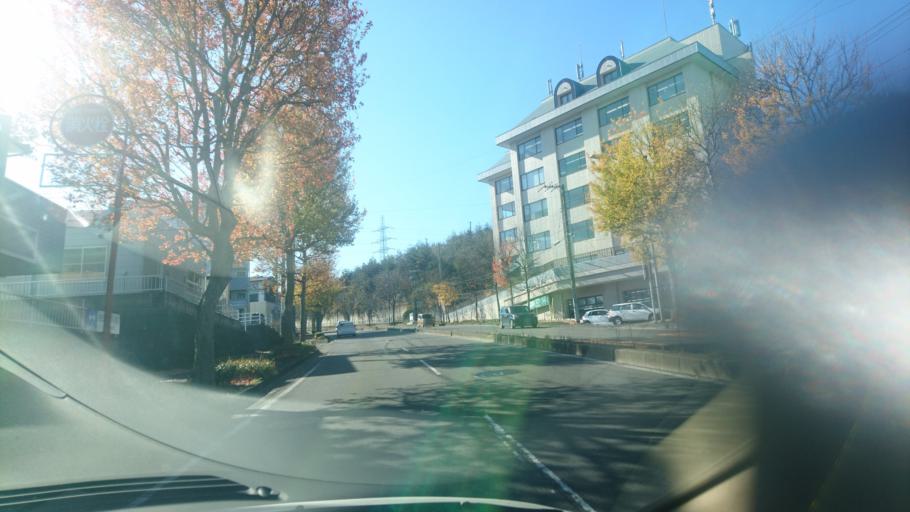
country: JP
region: Miyagi
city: Sendai-shi
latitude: 38.3052
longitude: 140.8320
